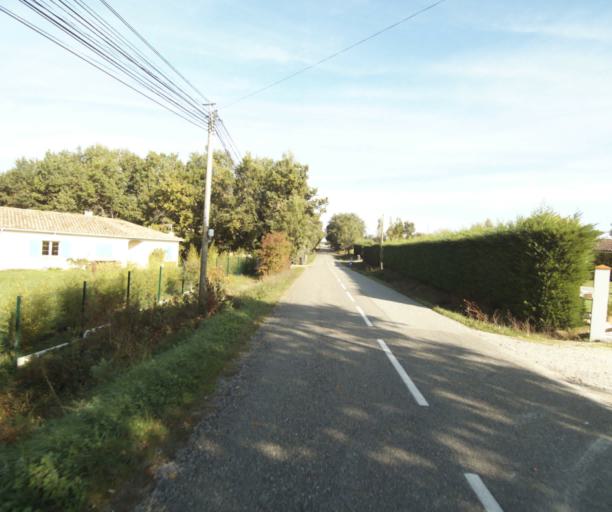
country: FR
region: Midi-Pyrenees
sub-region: Departement du Tarn-et-Garonne
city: Nohic
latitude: 43.9211
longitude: 1.4628
